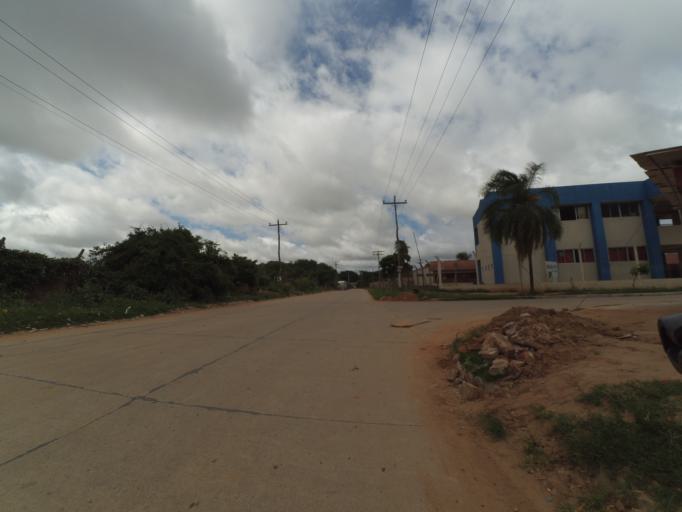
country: BO
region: Santa Cruz
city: Santa Cruz de la Sierra
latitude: -17.8731
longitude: -63.2337
